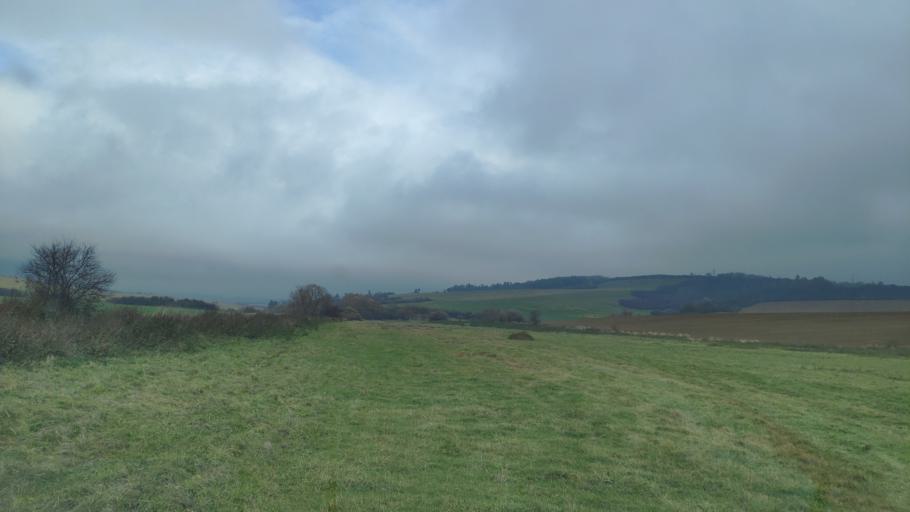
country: SK
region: Presovsky
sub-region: Okres Presov
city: Presov
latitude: 49.0140
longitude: 21.1995
